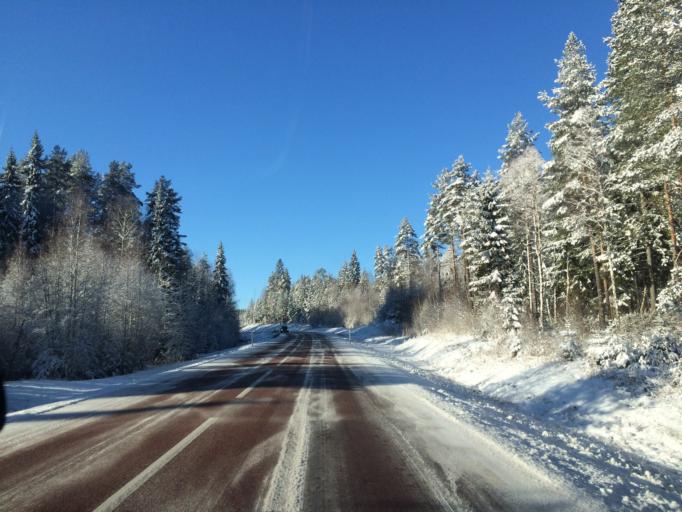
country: SE
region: Dalarna
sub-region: Mora Kommun
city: Mora
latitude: 60.8582
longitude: 14.3285
